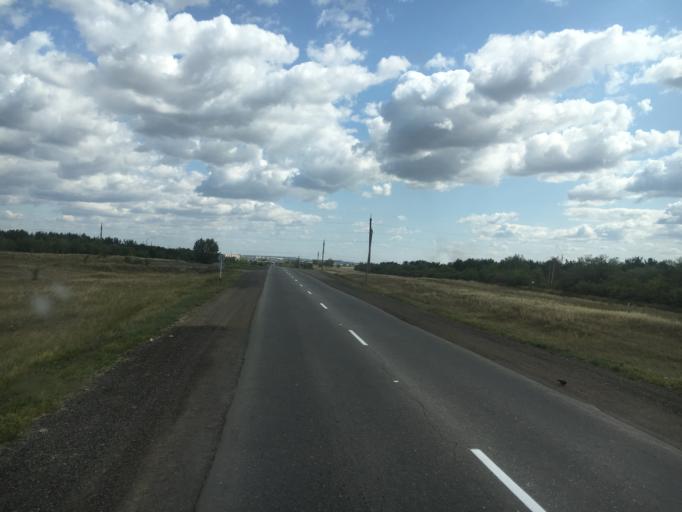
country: KZ
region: Qostanay
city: Rudnyy
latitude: 52.9373
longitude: 63.0241
